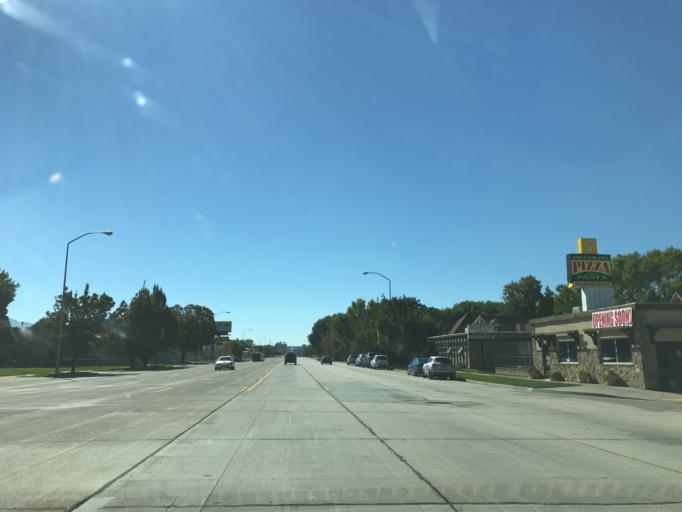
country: US
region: Utah
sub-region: Weber County
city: Ogden
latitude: 41.2429
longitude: -111.9700
